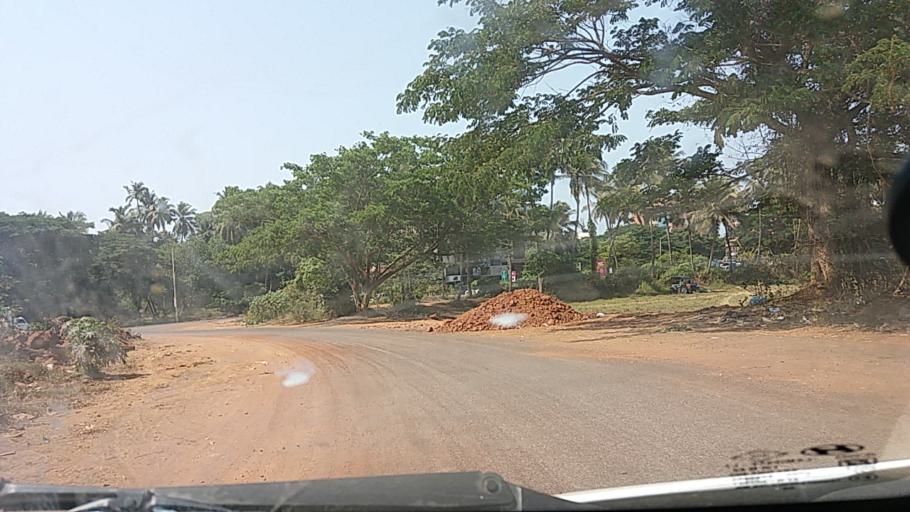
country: IN
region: Goa
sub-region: South Goa
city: Madgaon
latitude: 15.2821
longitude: 73.9554
